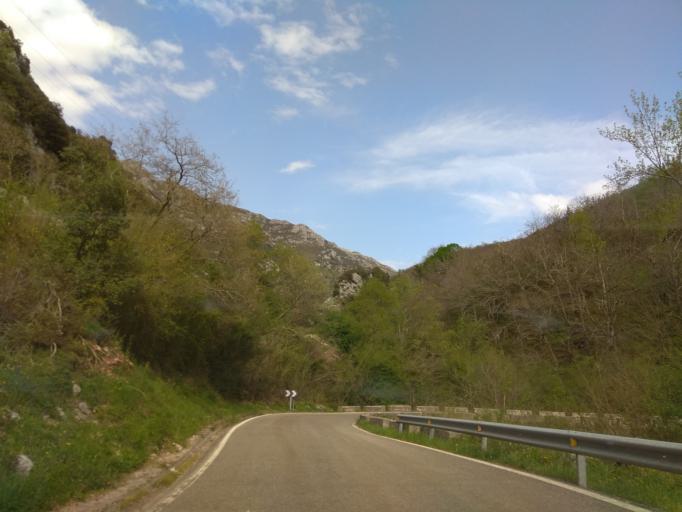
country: ES
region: Cantabria
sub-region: Provincia de Cantabria
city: Tresviso
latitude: 43.2547
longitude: -4.5695
